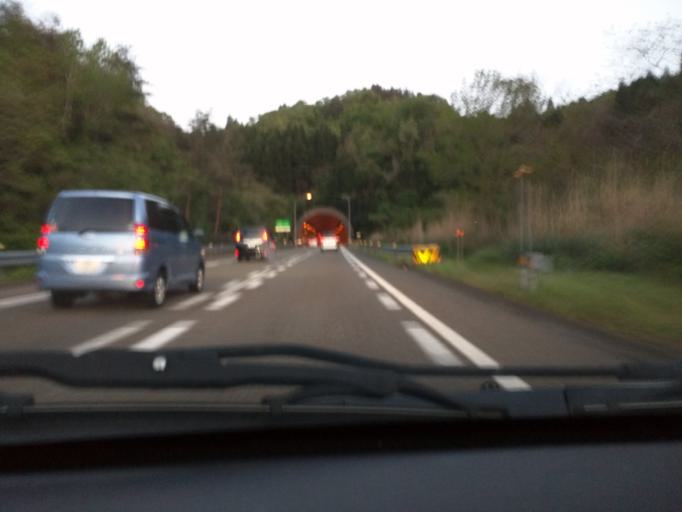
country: JP
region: Niigata
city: Kashiwazaki
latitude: 37.3441
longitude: 138.5144
